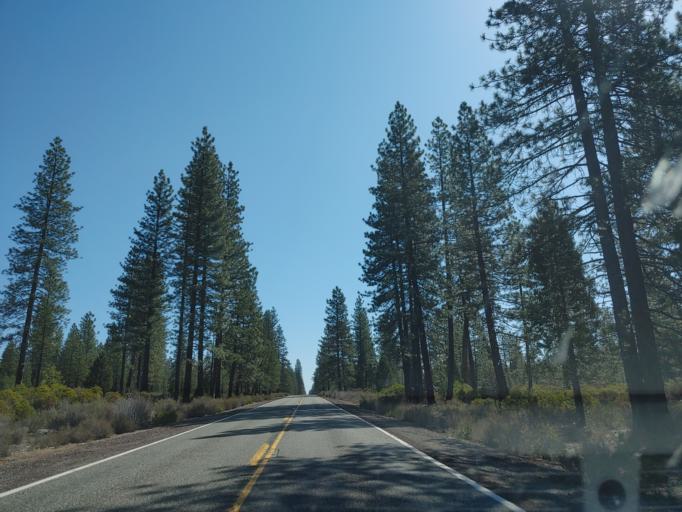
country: US
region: California
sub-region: Siskiyou County
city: McCloud
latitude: 41.2559
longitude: -122.0457
